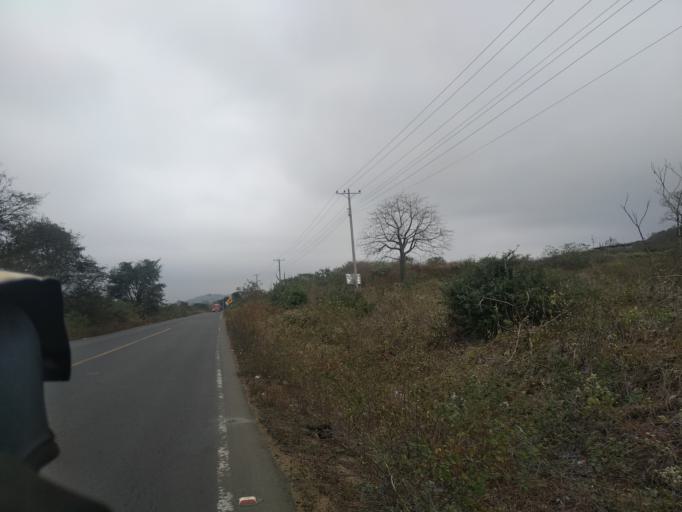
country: EC
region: Manabi
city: Montecristi
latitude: -1.0669
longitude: -80.6584
